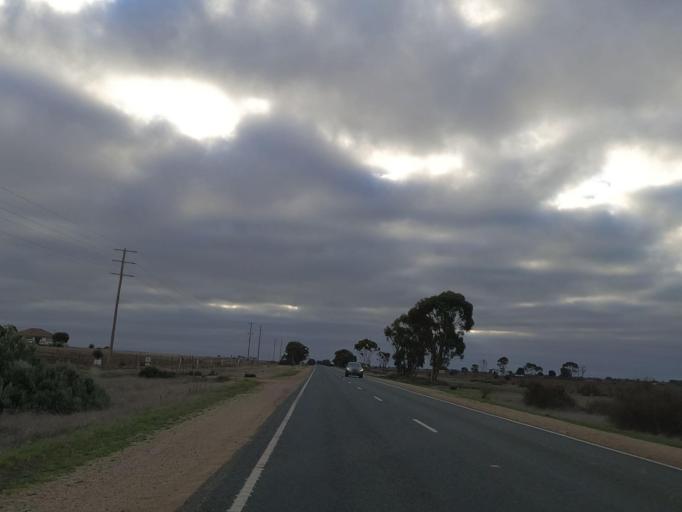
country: AU
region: Victoria
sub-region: Swan Hill
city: Swan Hill
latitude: -35.6423
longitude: 143.8306
